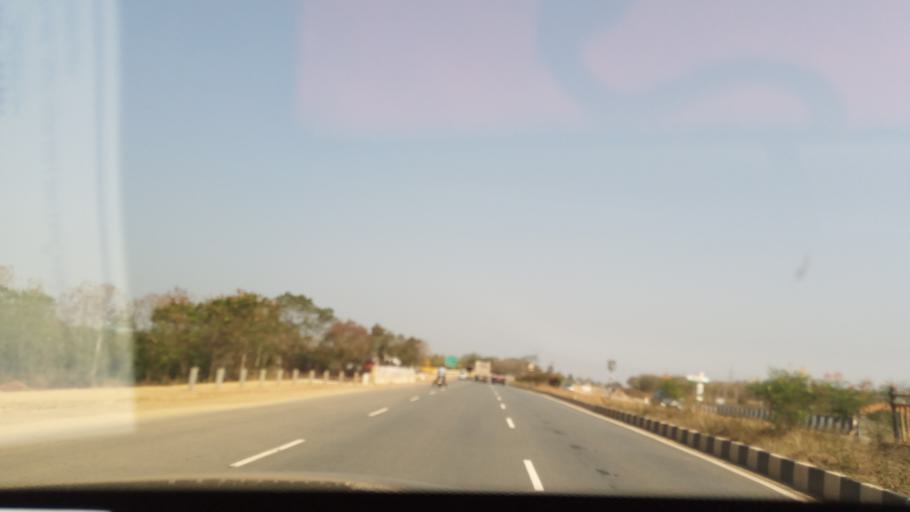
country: IN
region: Karnataka
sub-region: Dharwad
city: Kundgol
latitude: 15.2256
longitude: 75.1403
